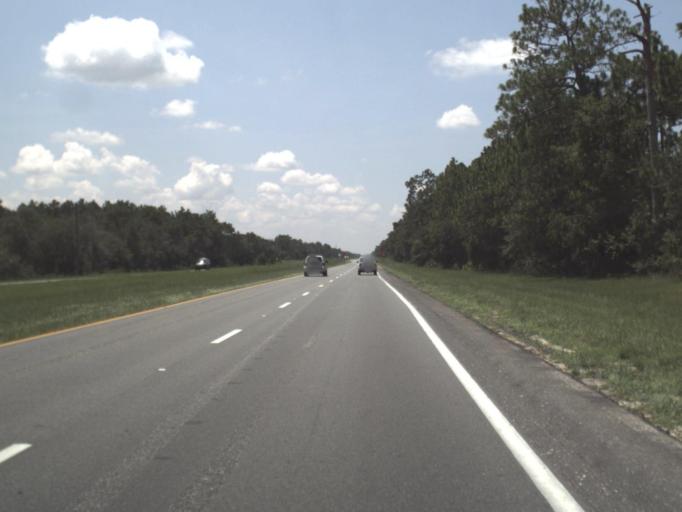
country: US
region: Florida
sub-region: Citrus County
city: Sugarmill Woods
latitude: 28.6634
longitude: -82.5524
